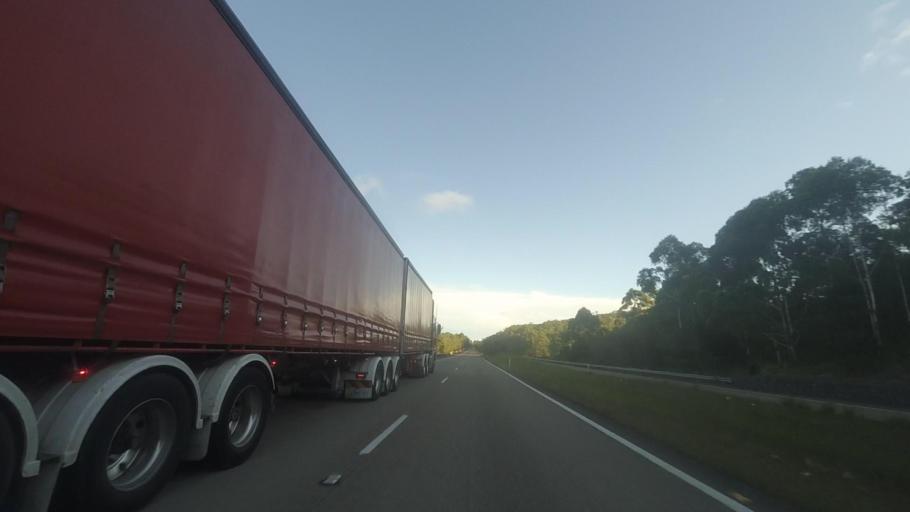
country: AU
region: New South Wales
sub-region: Great Lakes
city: Bulahdelah
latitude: -32.2889
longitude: 152.3417
